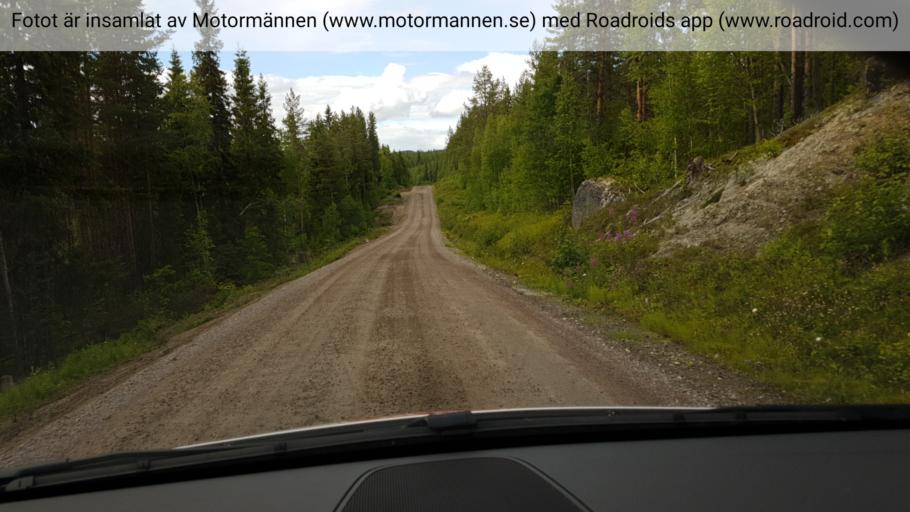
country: SE
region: Vaesterbotten
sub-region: Dorotea Kommun
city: Dorotea
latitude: 63.9675
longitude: 16.0684
